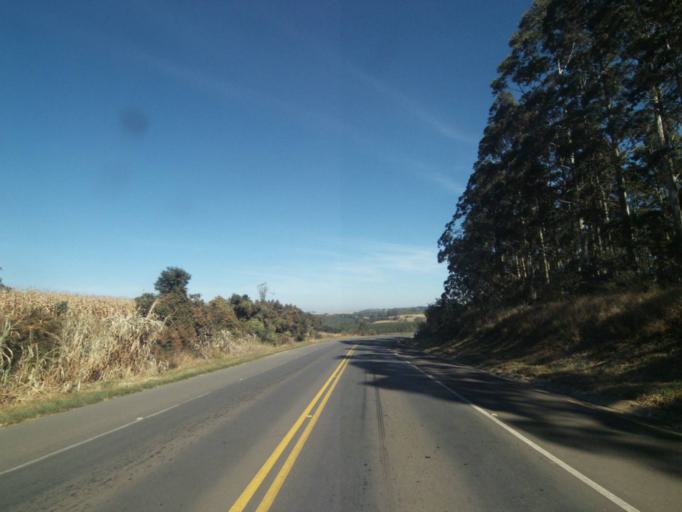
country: BR
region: Parana
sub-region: Tibagi
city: Tibagi
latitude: -24.8067
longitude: -50.4734
